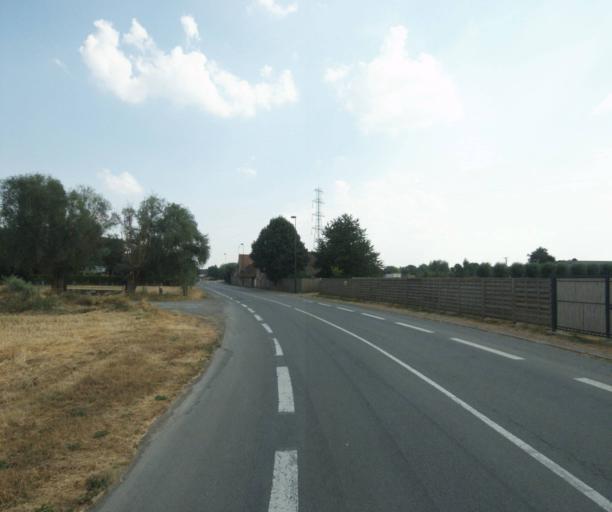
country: FR
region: Nord-Pas-de-Calais
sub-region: Departement du Nord
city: Linselles
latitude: 50.7222
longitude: 3.0806
